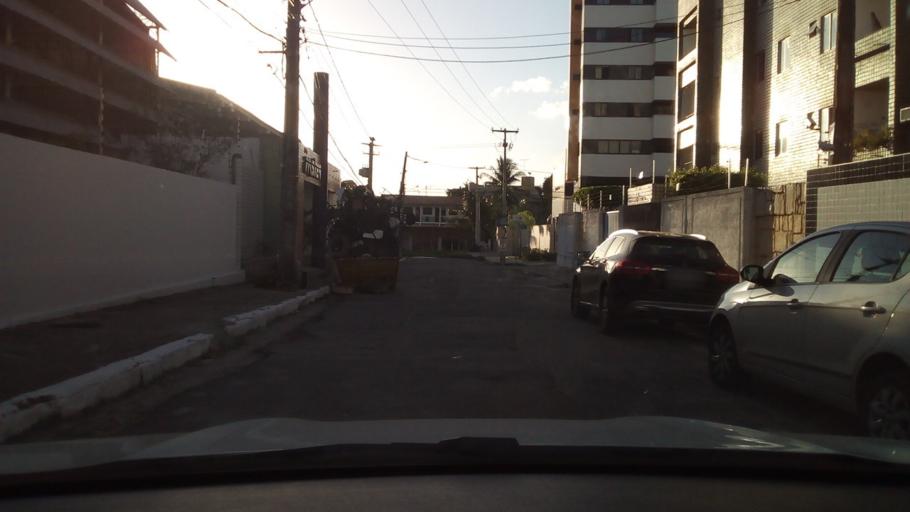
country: BR
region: Paraiba
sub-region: Joao Pessoa
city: Joao Pessoa
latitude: -7.0953
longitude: -34.8452
